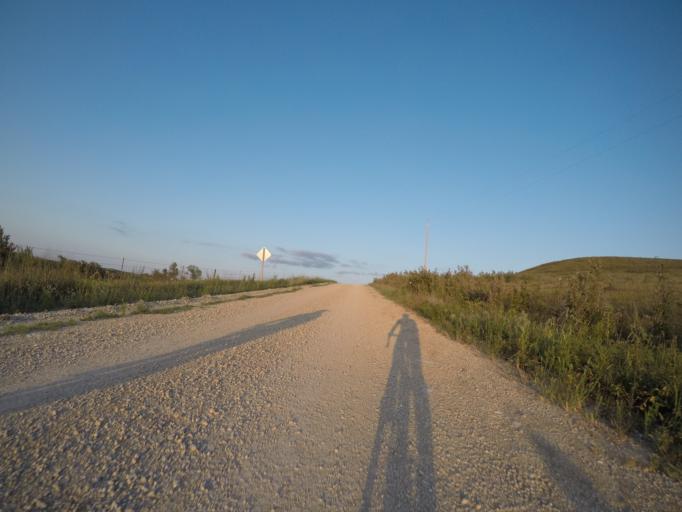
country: US
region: Kansas
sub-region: Riley County
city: Ogden
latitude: 39.0065
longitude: -96.6095
